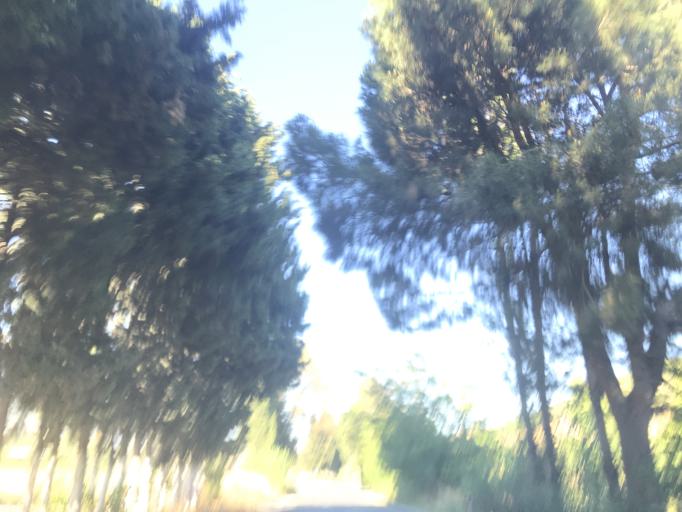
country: TR
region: Aydin
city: Soeke
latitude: 37.7515
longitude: 27.3618
